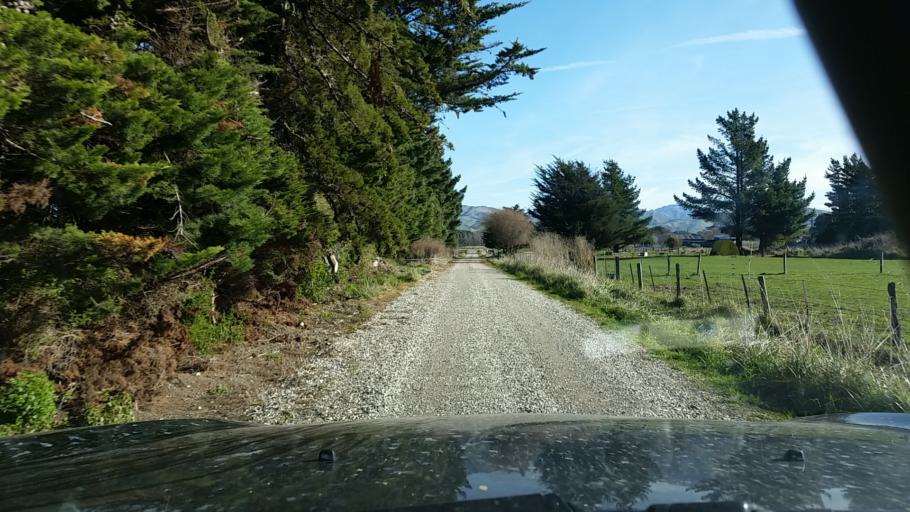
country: NZ
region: Marlborough
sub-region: Marlborough District
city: Blenheim
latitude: -41.8272
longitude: 174.1532
